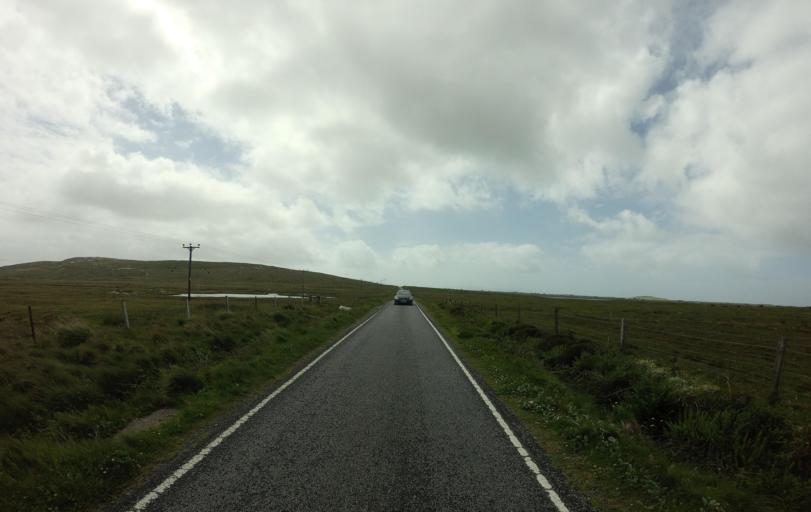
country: GB
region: Scotland
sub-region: Eilean Siar
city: Isle of South Uist
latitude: 57.1515
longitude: -7.3715
